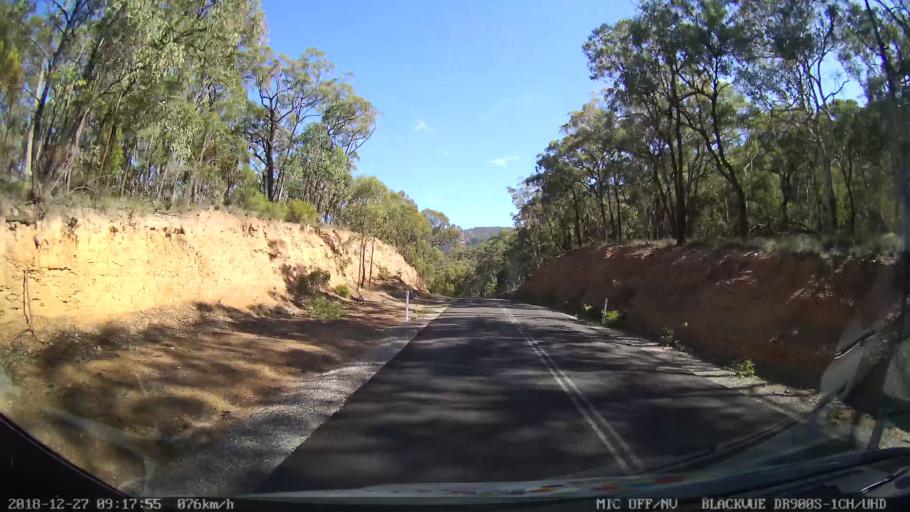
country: AU
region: New South Wales
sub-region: Lithgow
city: Portland
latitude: -33.1326
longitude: 150.0461
